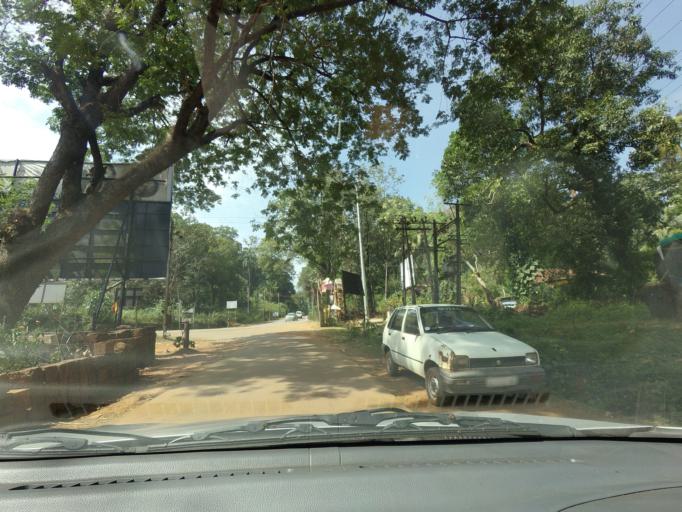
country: IN
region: Karnataka
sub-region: Dakshina Kannada
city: Sulya
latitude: 12.6873
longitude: 75.6083
